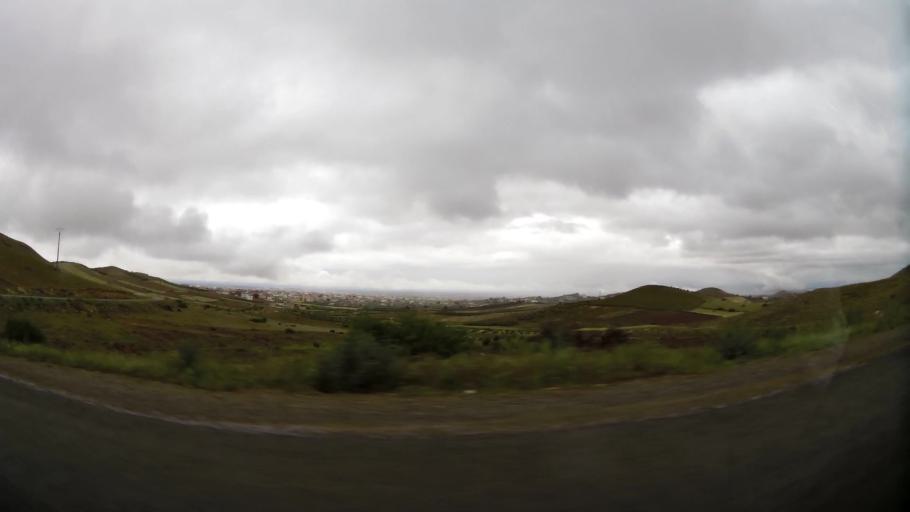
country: MA
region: Oriental
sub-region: Nador
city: Midar
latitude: 35.0669
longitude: -3.4759
